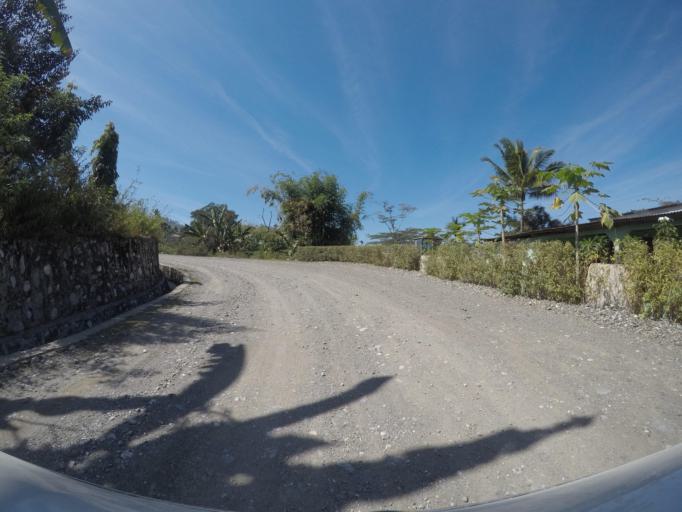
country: TL
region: Ermera
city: Gleno
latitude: -8.8091
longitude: 125.3170
